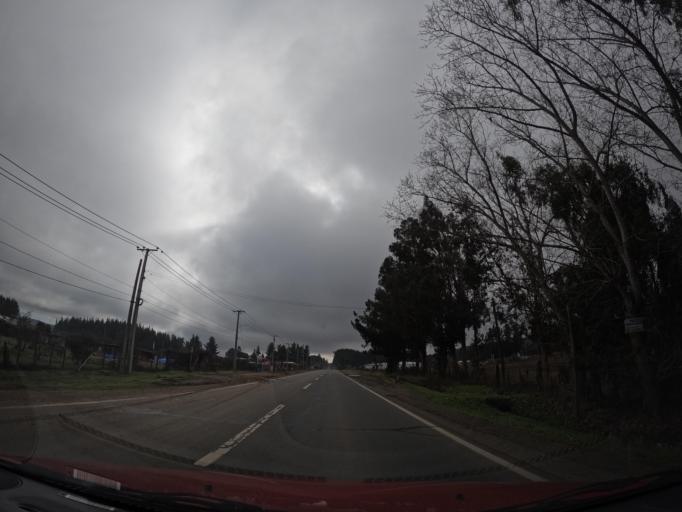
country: CL
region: Maule
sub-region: Provincia de Cauquenes
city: Cauquenes
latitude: -36.2628
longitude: -72.5481
